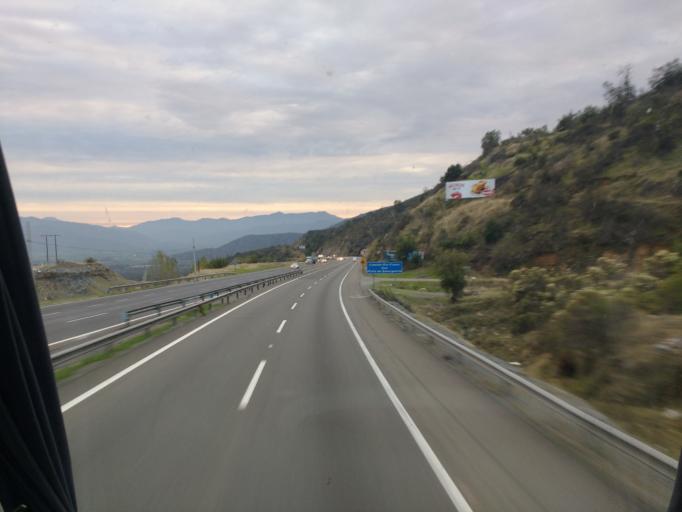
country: CL
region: Santiago Metropolitan
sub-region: Provincia de Talagante
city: Penaflor
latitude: -33.4580
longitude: -70.9668
